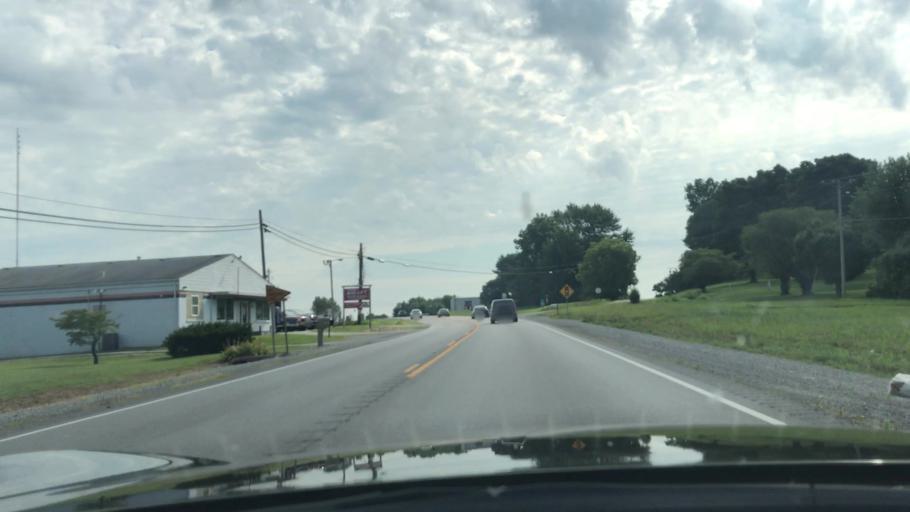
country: US
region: Kentucky
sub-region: Taylor County
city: Campbellsville
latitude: 37.3322
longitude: -85.3793
